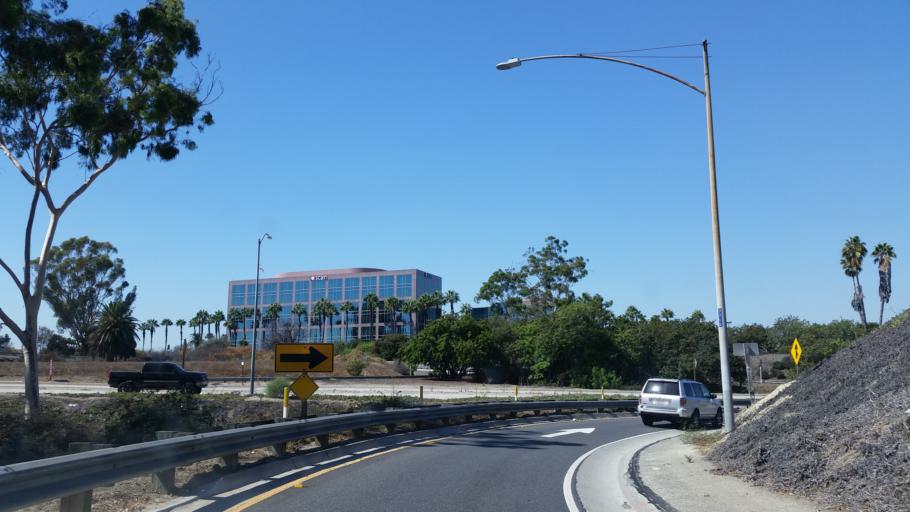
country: US
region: California
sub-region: Los Angeles County
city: Signal Hill
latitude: 33.8066
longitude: -118.1417
